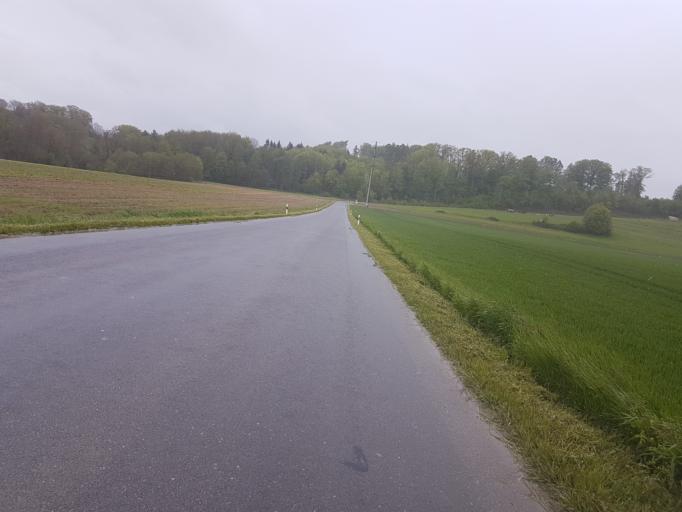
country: CH
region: Vaud
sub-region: Gros-de-Vaud District
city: Penthalaz
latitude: 46.6238
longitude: 6.5286
